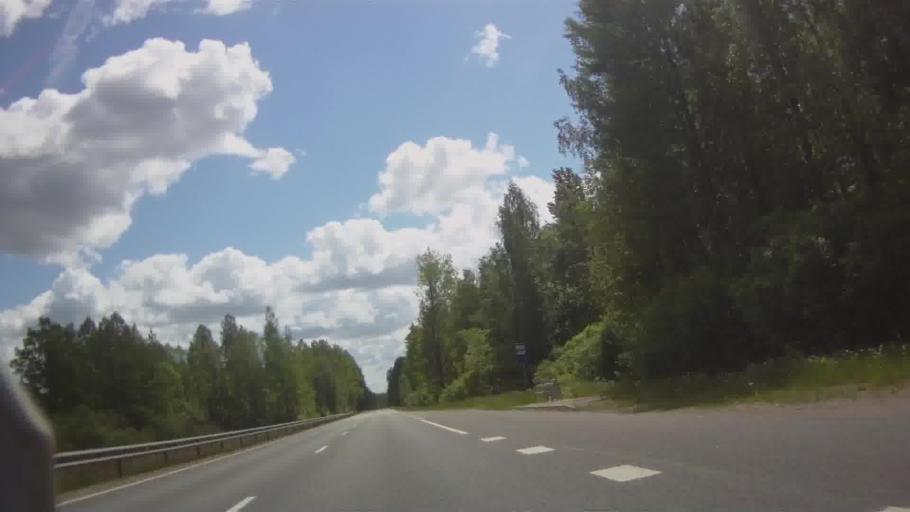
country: LV
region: Livani
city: Livani
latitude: 56.5420
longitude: 26.1254
